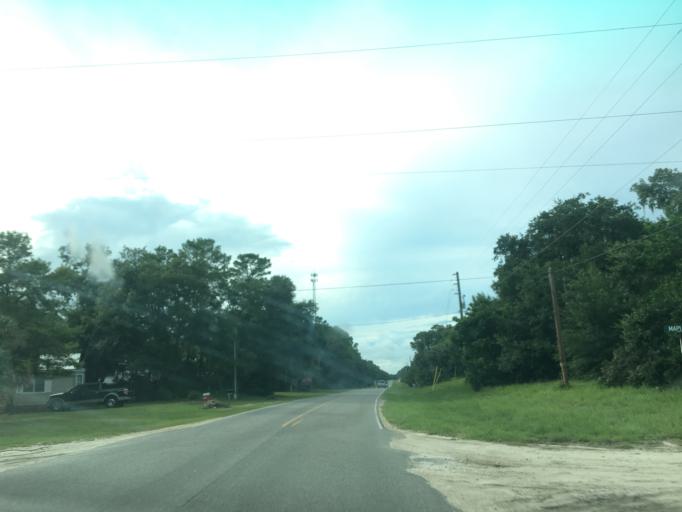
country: US
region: Florida
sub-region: Wakulla County
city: Crawfordville
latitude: 29.9132
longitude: -84.3664
